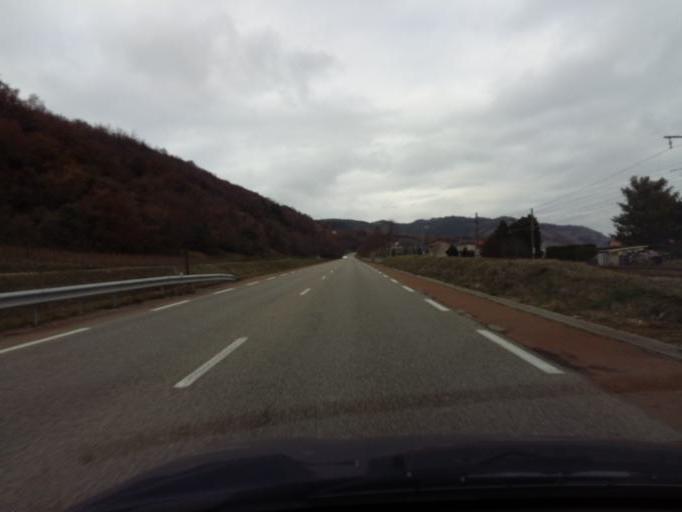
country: FR
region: Rhone-Alpes
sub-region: Departement de l'Ardeche
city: Mauves
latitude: 45.0296
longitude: 4.8291
